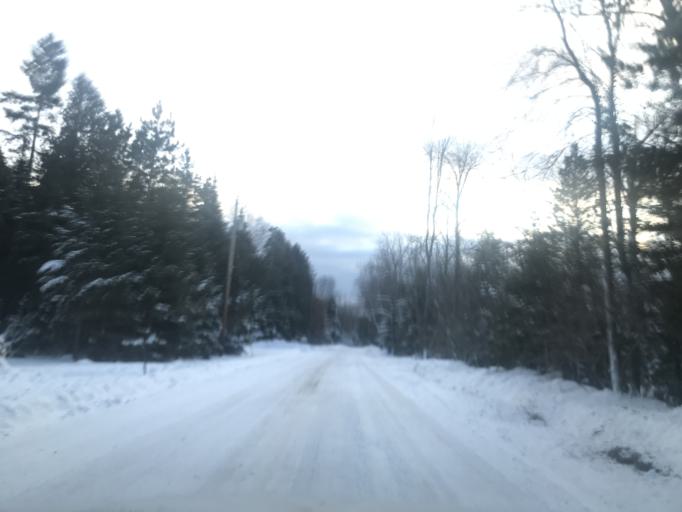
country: US
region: Michigan
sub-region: Menominee County
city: Menominee
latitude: 45.4214
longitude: -87.3337
